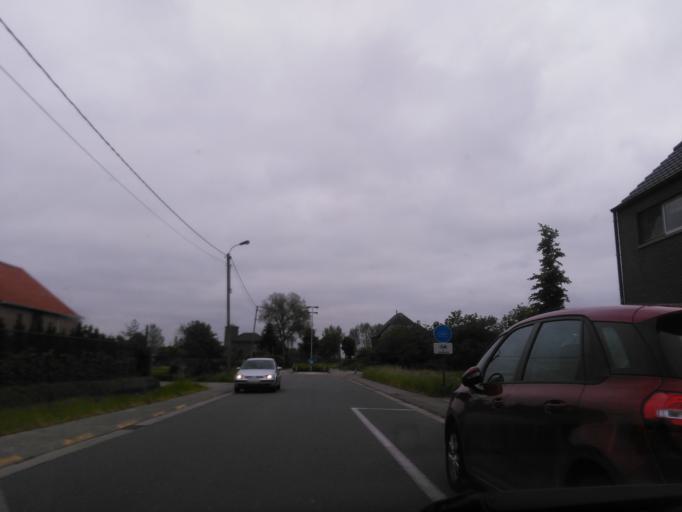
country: BE
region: Flanders
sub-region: Provincie Oost-Vlaanderen
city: Beveren
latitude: 51.2008
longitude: 4.2654
